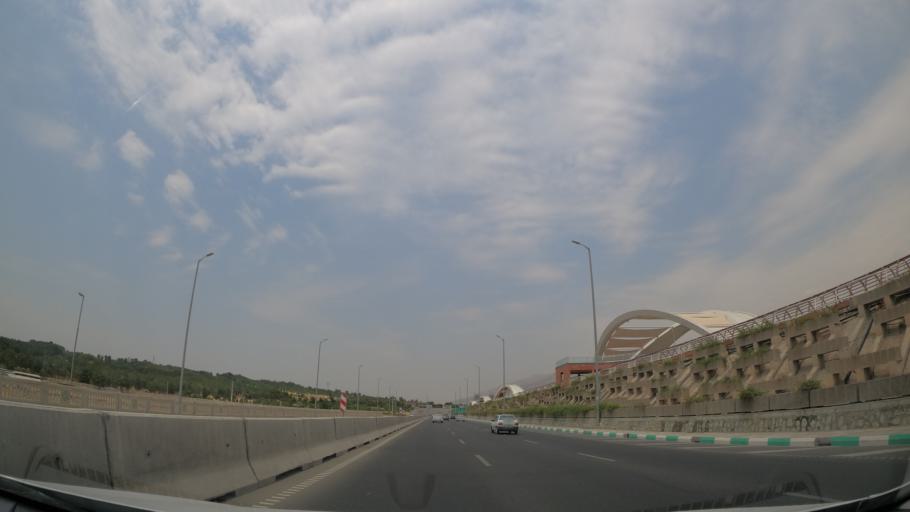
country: IR
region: Tehran
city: Shahr-e Qods
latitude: 35.7395
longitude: 51.2149
